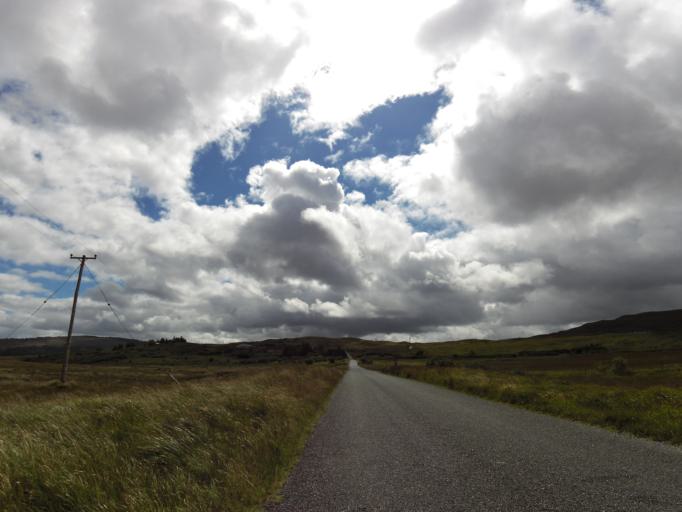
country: IE
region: Connaught
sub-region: County Galway
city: Oughterard
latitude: 53.4027
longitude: -9.3321
